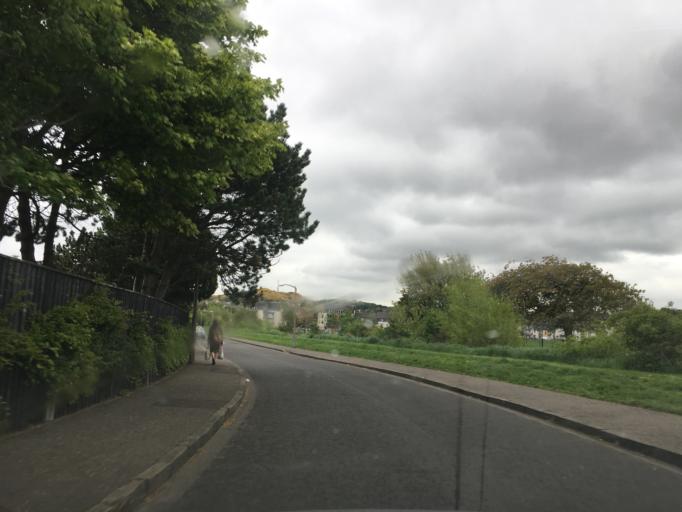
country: GB
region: Scotland
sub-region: Edinburgh
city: Colinton
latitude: 55.9121
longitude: -3.2296
